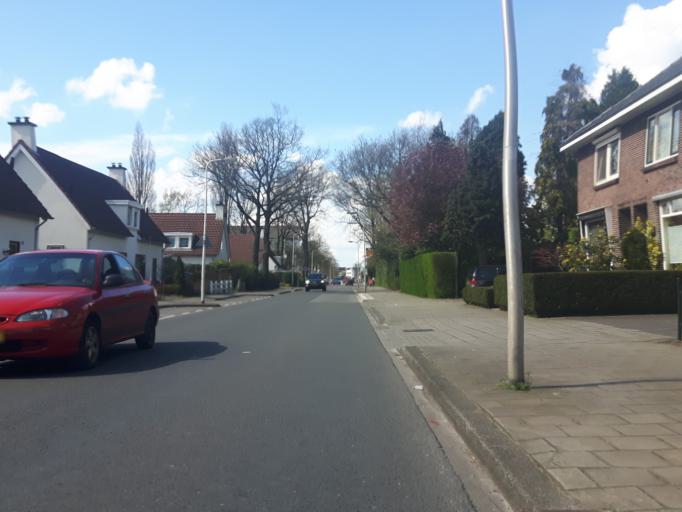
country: NL
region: Overijssel
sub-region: Gemeente Enschede
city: Enschede
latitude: 52.2316
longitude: 6.8539
